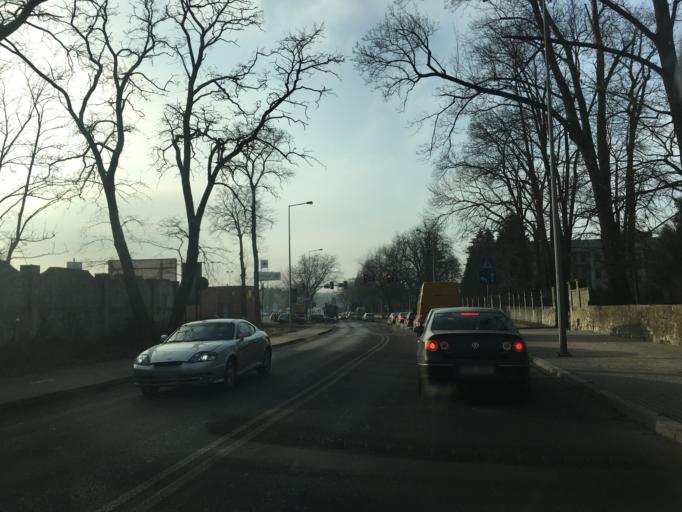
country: PL
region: Lower Silesian Voivodeship
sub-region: Powiat boleslawiecki
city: Boleslawiec
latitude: 51.2650
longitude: 15.5542
